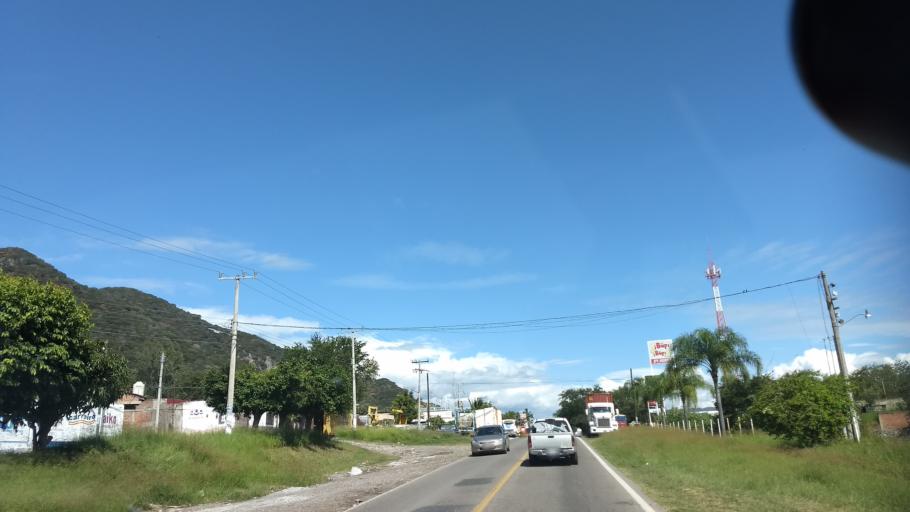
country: MX
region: Jalisco
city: Tuxpan
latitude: 19.5537
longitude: -103.3901
